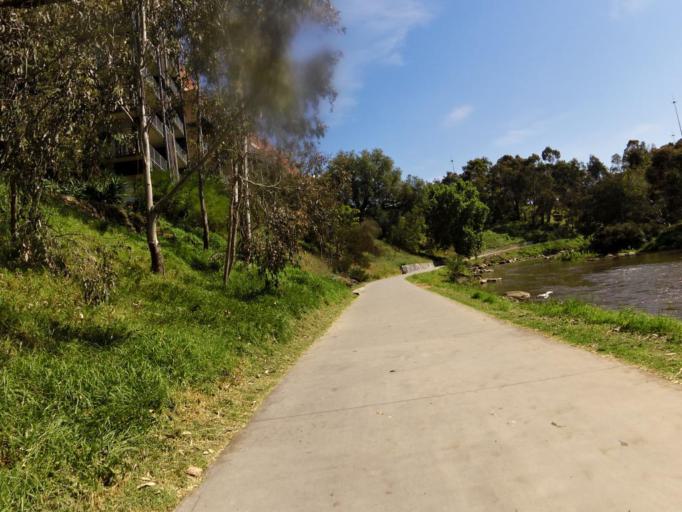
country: AU
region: Victoria
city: Abbotsford
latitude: -37.7981
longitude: 144.9996
